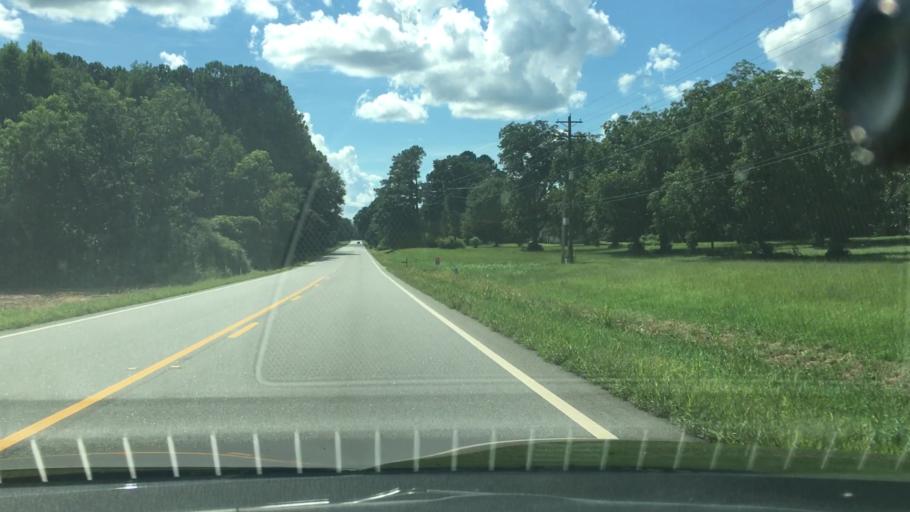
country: US
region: Georgia
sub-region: Butts County
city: Indian Springs
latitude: 33.2882
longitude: -83.9022
